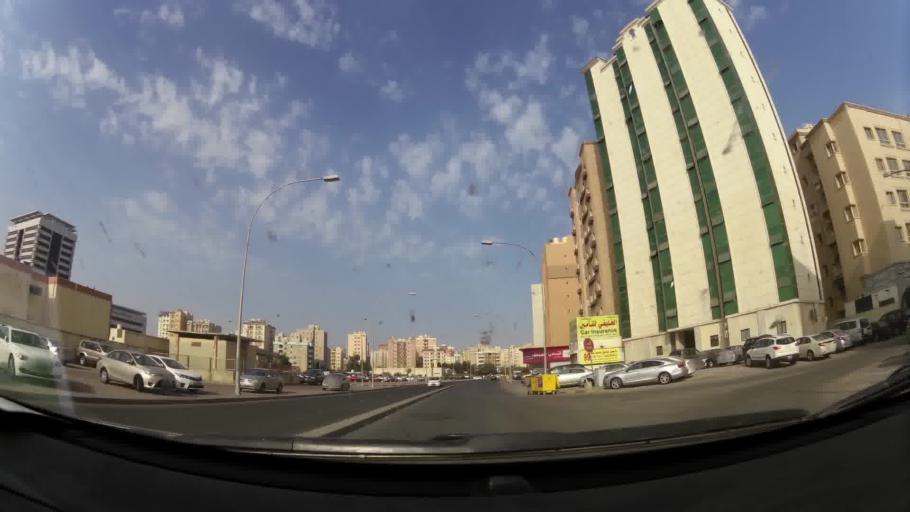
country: KW
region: Muhafazat Hawalli
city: As Salimiyah
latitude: 29.3314
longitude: 48.0840
